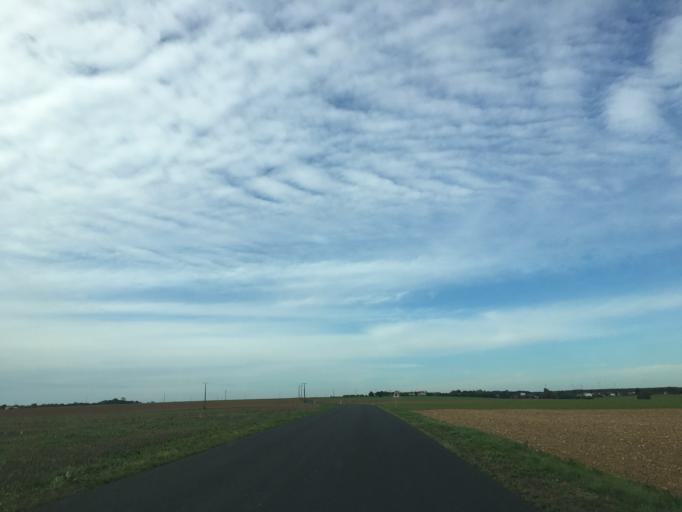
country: FR
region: Poitou-Charentes
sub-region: Departement des Deux-Sevres
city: Beauvoir-sur-Niort
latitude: 46.0710
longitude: -0.4899
